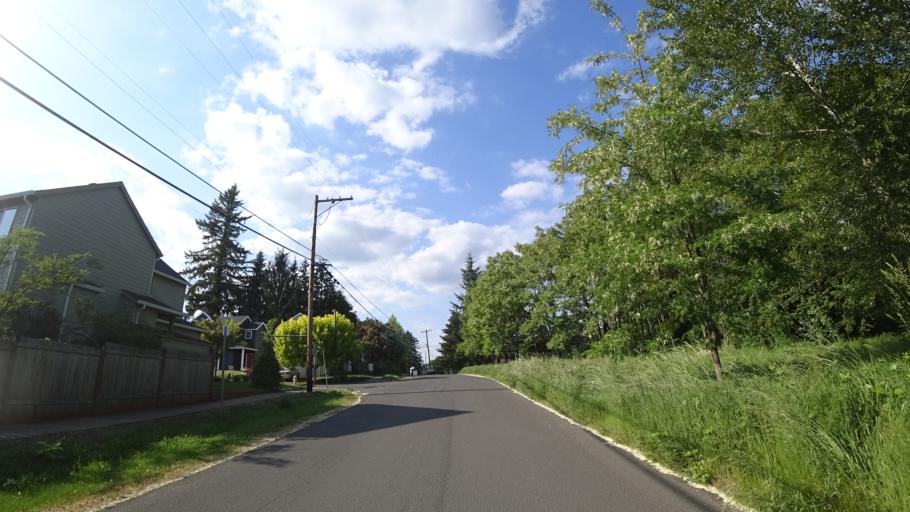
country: US
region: Oregon
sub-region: Washington County
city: Garden Home-Whitford
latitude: 45.4644
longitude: -122.7482
